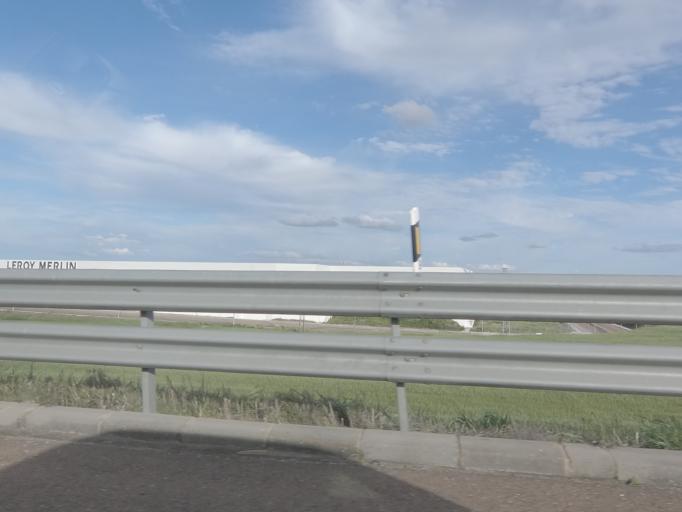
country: ES
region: Extremadura
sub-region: Provincia de Badajoz
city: Badajoz
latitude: 38.9027
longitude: -6.9999
